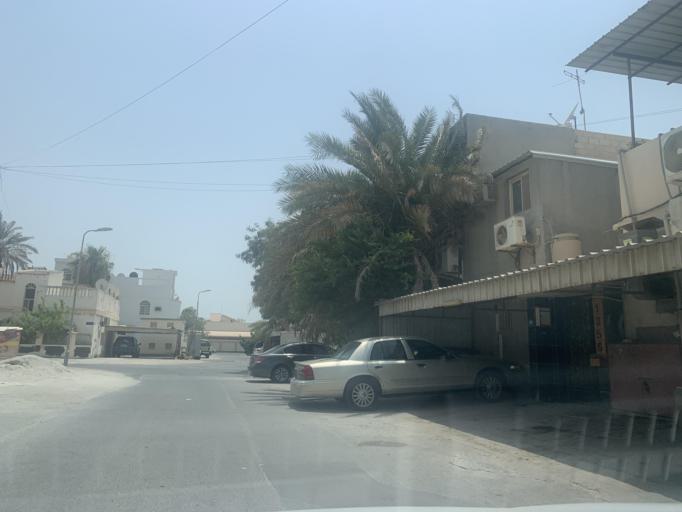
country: BH
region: Manama
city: Jidd Hafs
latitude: 26.2227
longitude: 50.4631
